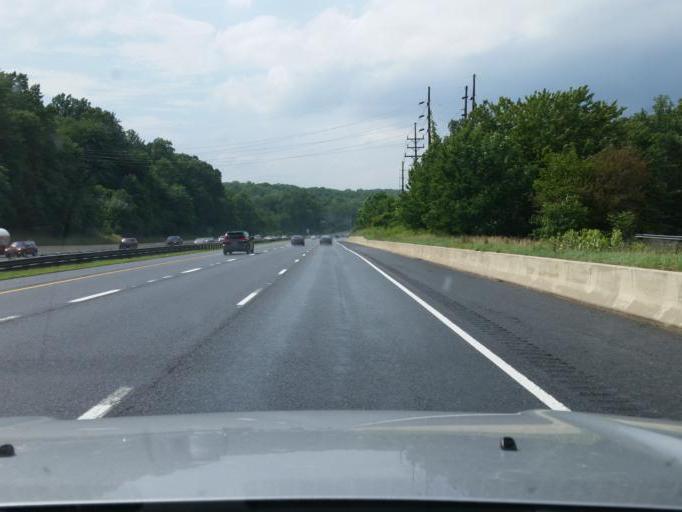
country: US
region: Maryland
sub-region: Montgomery County
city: Germantown
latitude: 39.2038
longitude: -77.2696
